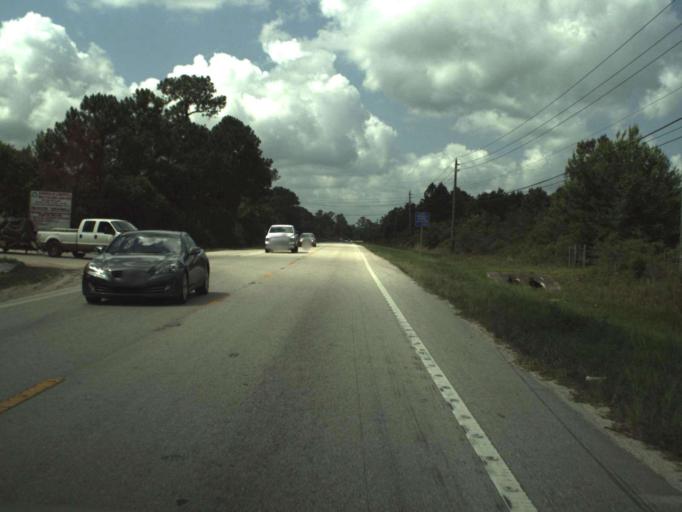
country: US
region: Florida
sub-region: Volusia County
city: Samsula-Spruce Creek
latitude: 28.9912
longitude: -81.0720
